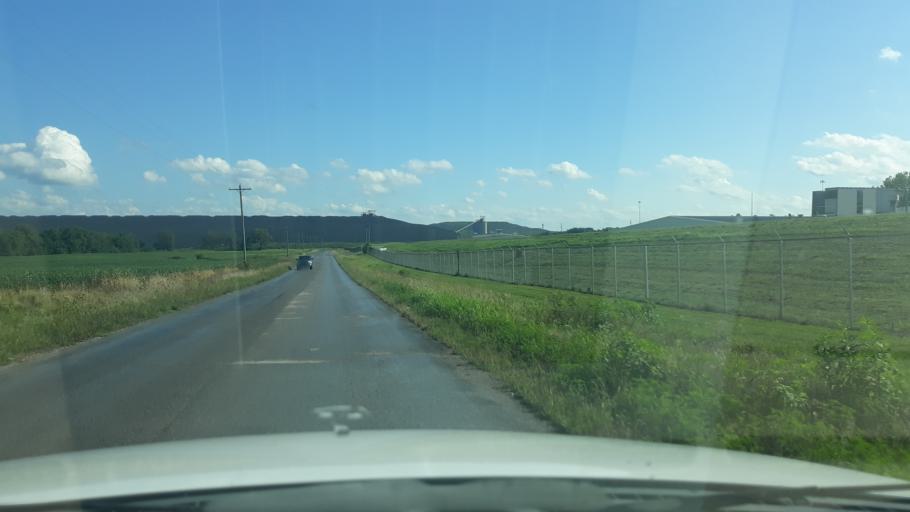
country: US
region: Illinois
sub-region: Saline County
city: Harrisburg
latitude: 37.8404
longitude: -88.5814
